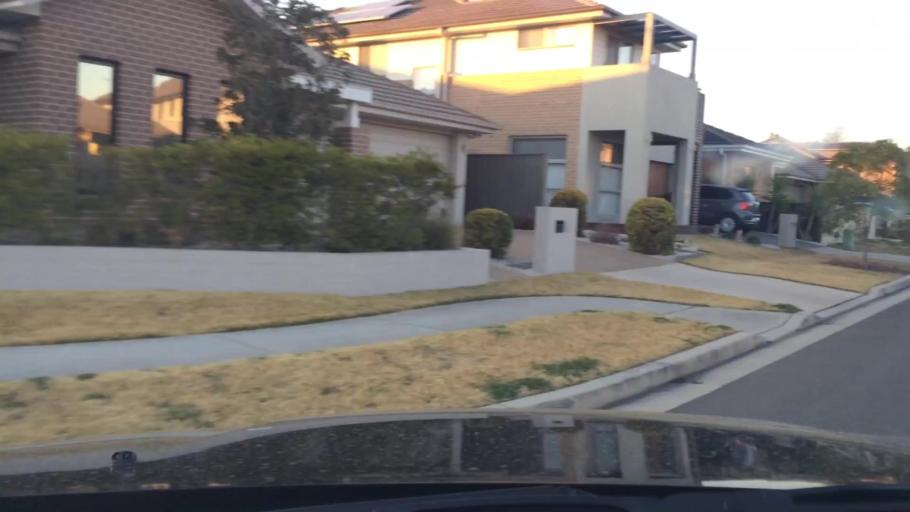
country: AU
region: New South Wales
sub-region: Bankstown
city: Milperra
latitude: -33.9396
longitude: 150.9557
